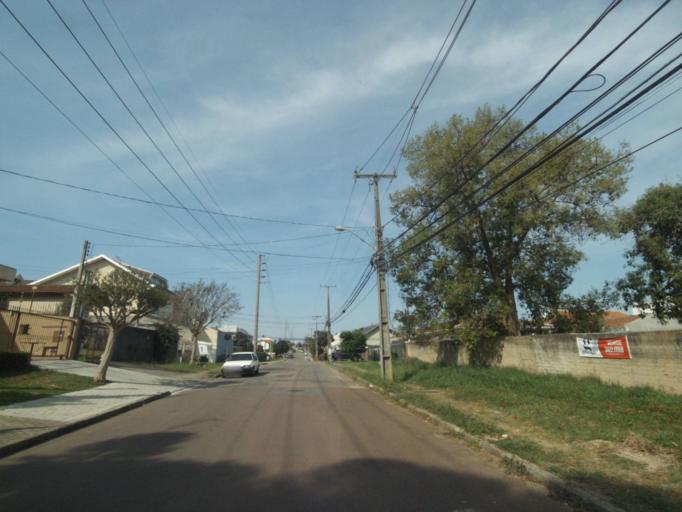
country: BR
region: Parana
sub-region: Curitiba
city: Curitiba
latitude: -25.4603
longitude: -49.3108
